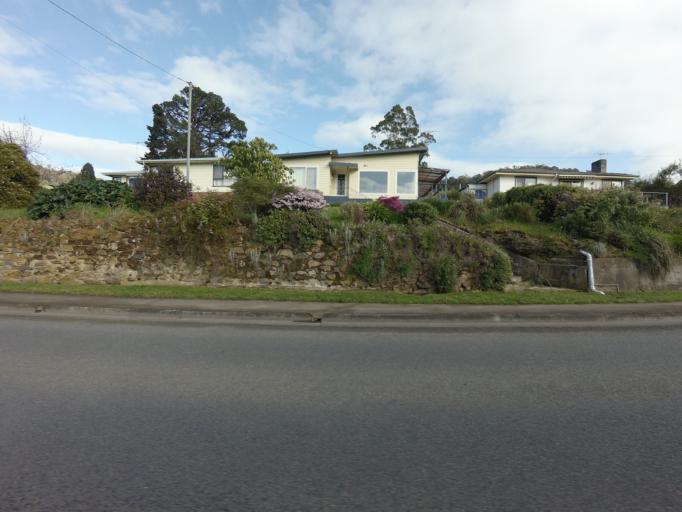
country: AU
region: Tasmania
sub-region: Huon Valley
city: Franklin
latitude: -43.0846
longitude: 147.0145
